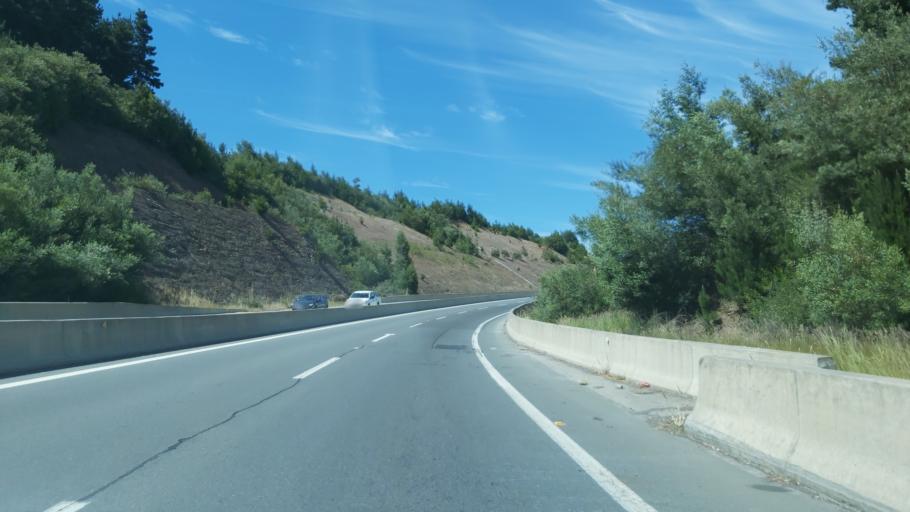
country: CL
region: Biobio
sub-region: Provincia de Concepcion
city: Lota
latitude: -37.0895
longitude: -73.1376
